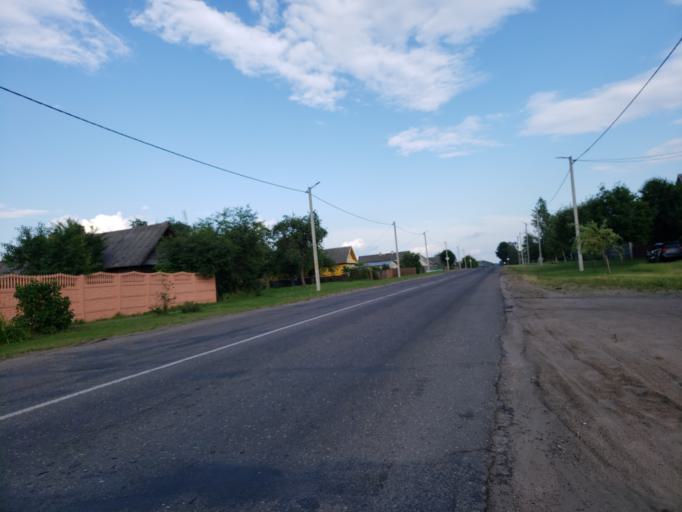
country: BY
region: Minsk
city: Chervyen'
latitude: 53.7025
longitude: 28.4415
